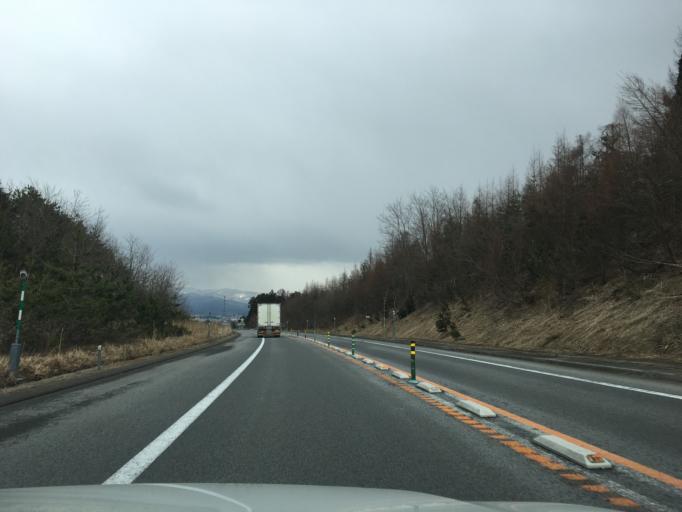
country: JP
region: Aomori
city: Aomori Shi
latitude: 40.7981
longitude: 140.7035
